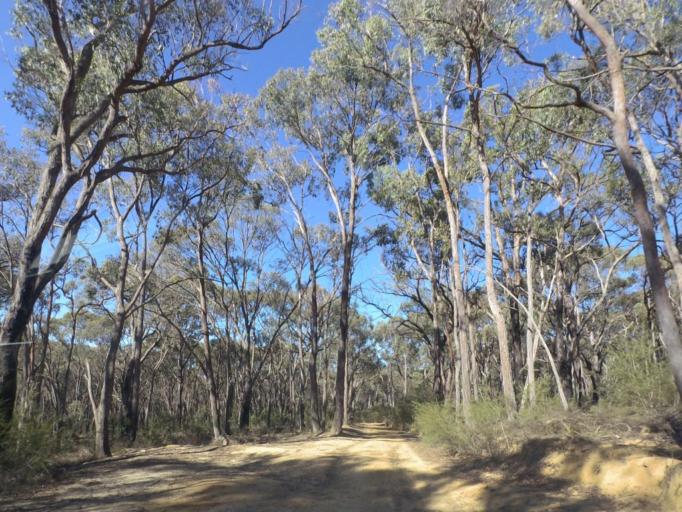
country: AU
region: Victoria
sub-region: Murrindindi
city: Kinglake West
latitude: -37.4640
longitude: 145.3697
